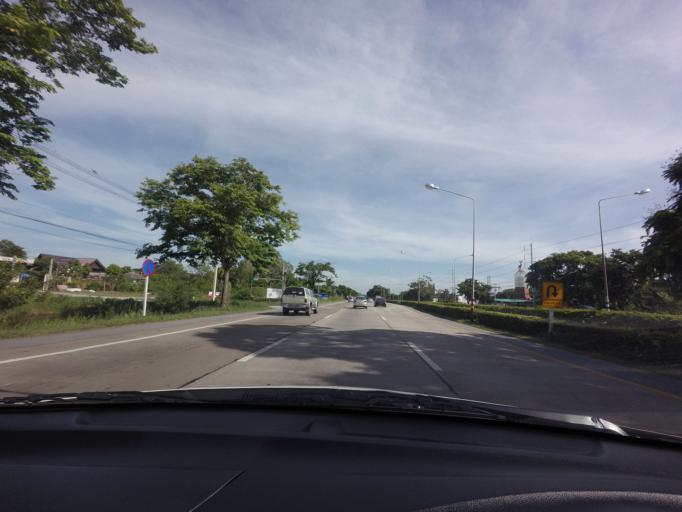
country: TH
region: Suphan Buri
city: Bang Pla Ma
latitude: 14.4324
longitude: 100.1419
